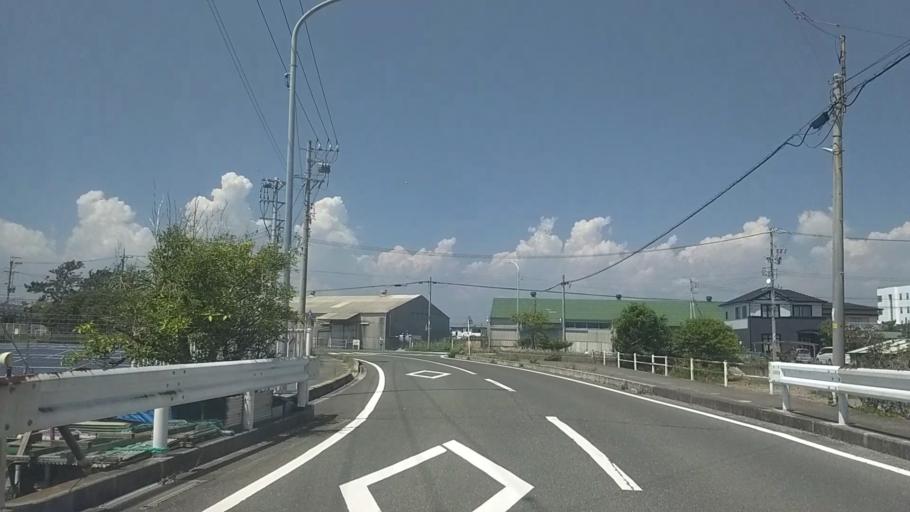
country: JP
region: Shizuoka
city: Kosai-shi
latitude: 34.6851
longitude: 137.5779
